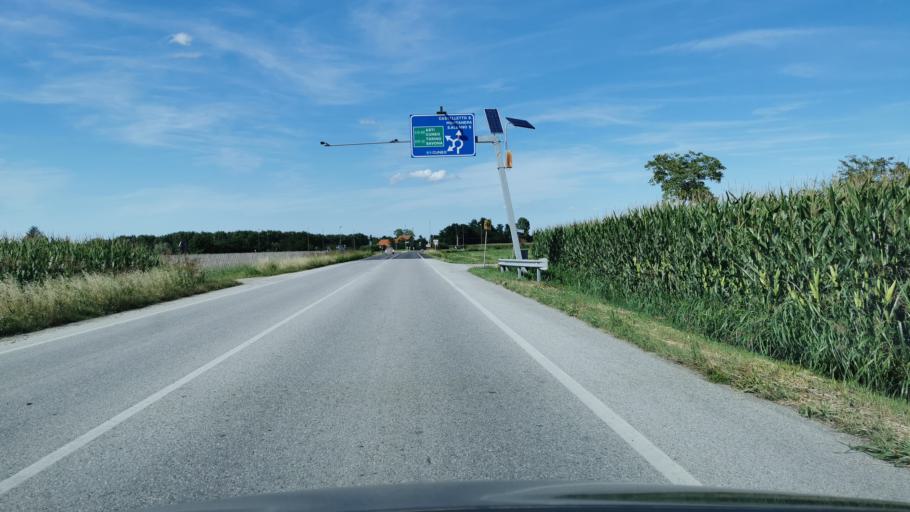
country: IT
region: Piedmont
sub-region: Provincia di Cuneo
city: Cuneo
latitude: 44.4128
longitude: 7.5953
